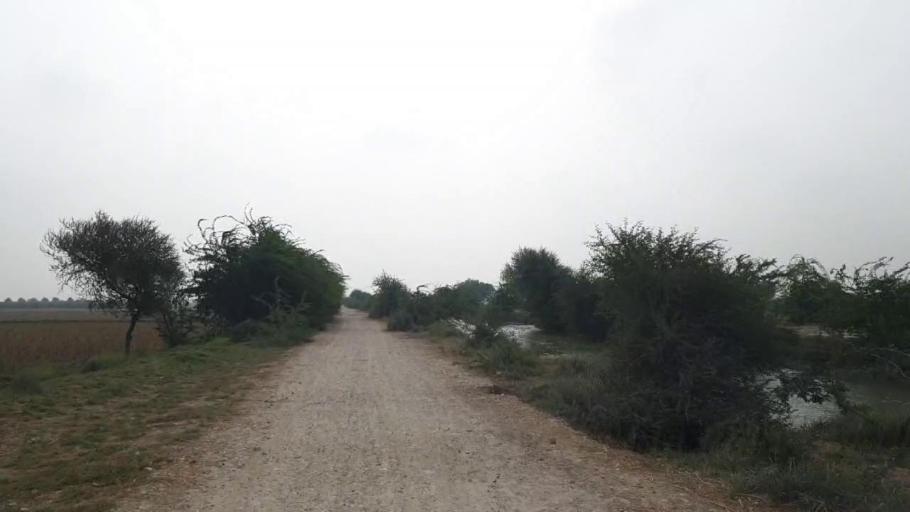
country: PK
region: Sindh
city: Kario
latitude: 24.8540
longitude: 68.5277
